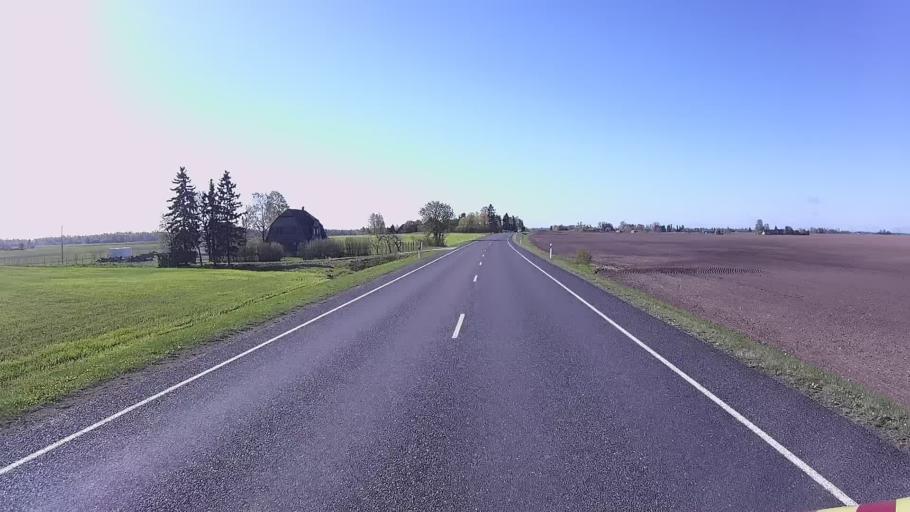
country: EE
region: Viljandimaa
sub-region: Vohma linn
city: Vohma
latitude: 58.6710
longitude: 25.6063
